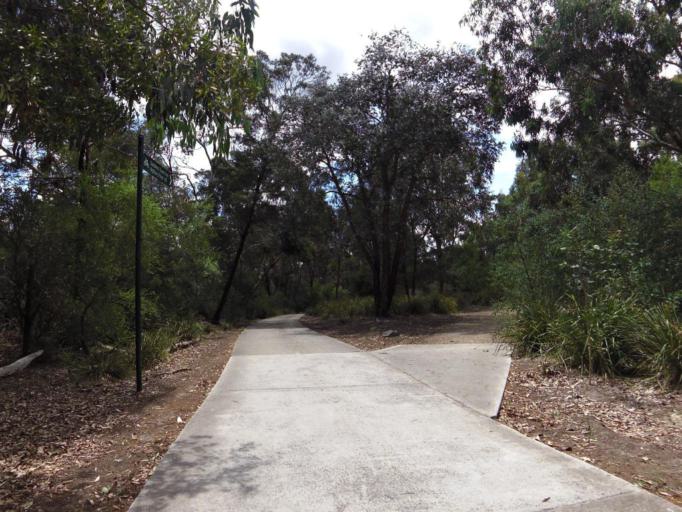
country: AU
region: Victoria
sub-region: Monash
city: Ashwood
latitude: -37.8580
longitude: 145.1021
